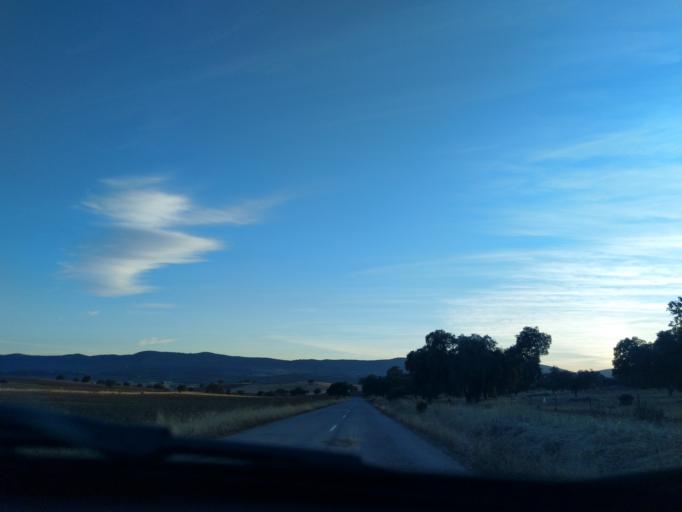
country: ES
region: Extremadura
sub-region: Provincia de Badajoz
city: Valverde de Llerena
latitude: 38.1935
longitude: -5.8541
